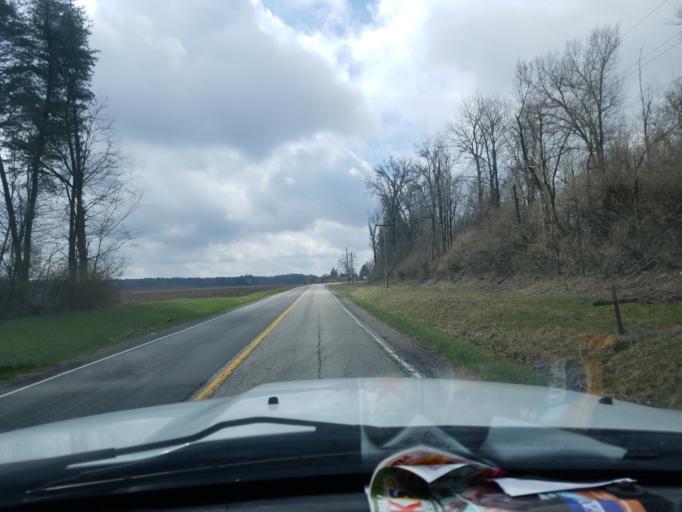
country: US
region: Indiana
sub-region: Sullivan County
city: Farmersburg
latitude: 39.3588
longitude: -87.3054
